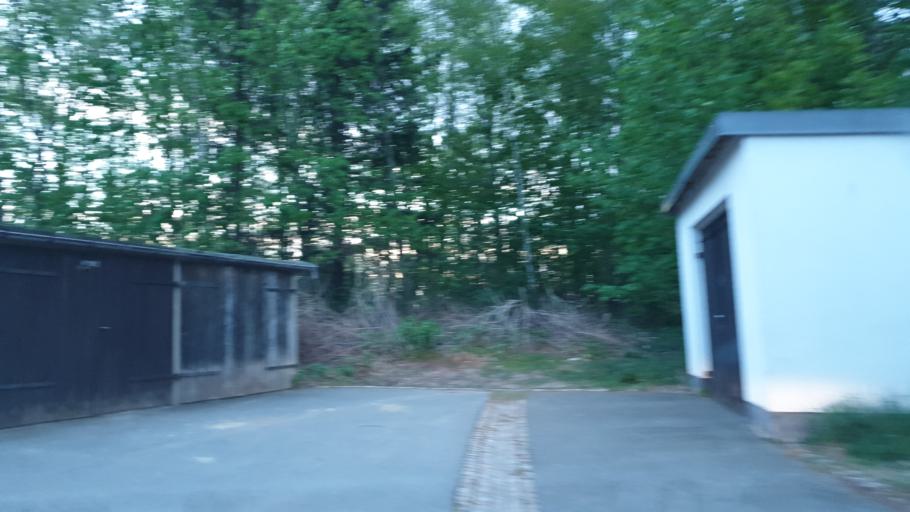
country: DE
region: Saxony
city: Hohndorf
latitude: 50.7337
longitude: 12.6750
